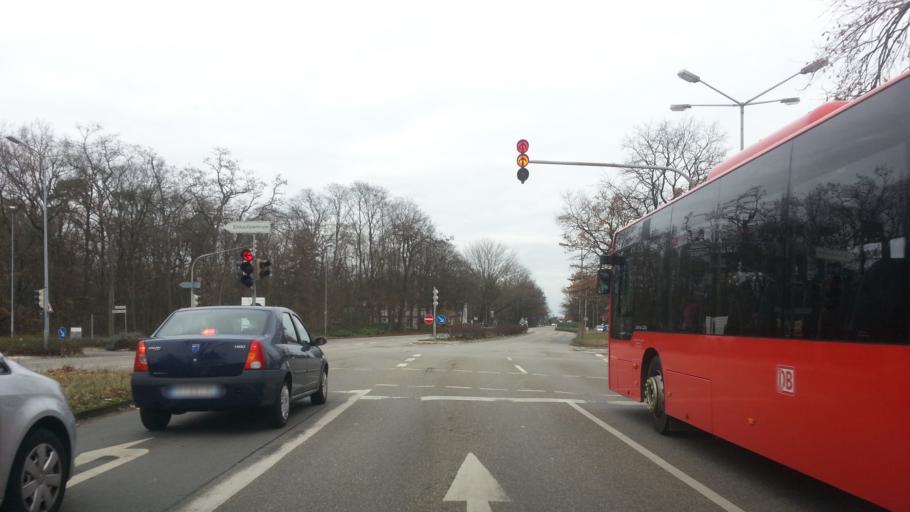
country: DE
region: Baden-Wuerttemberg
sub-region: Karlsruhe Region
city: Hockenheim
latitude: 49.3384
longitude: 8.5337
